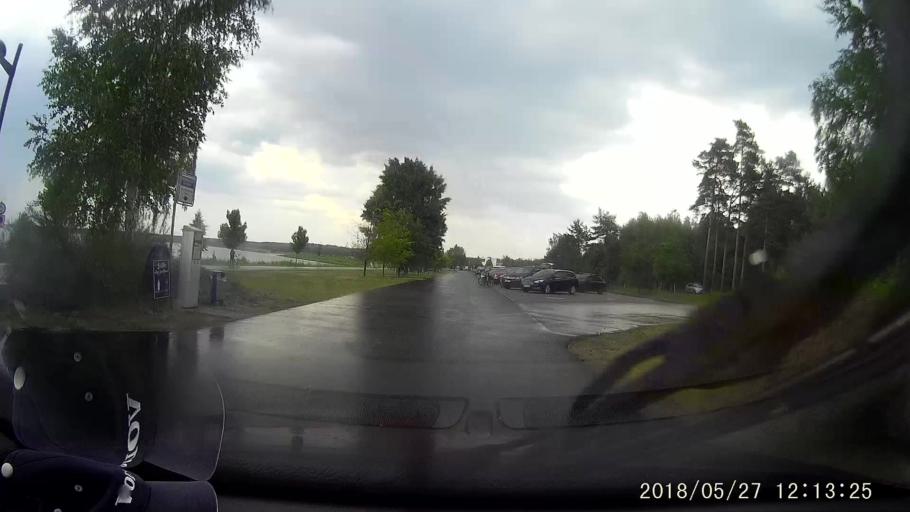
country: DE
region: Saxony
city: Uhyst
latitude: 51.3576
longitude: 14.5539
